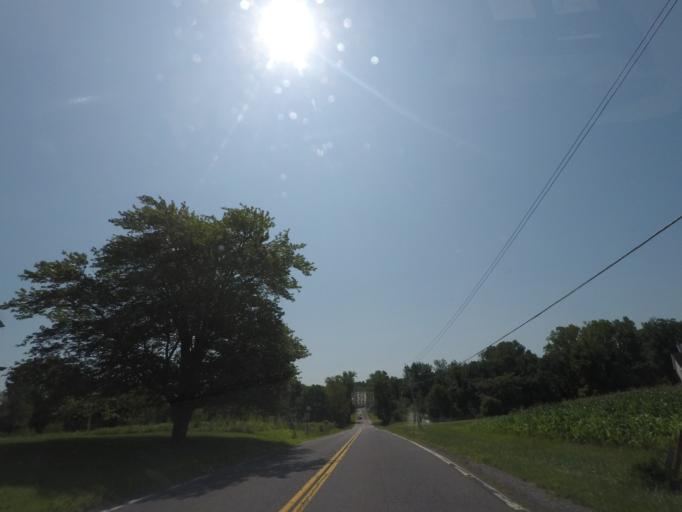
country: US
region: New York
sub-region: Saratoga County
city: Mechanicville
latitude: 42.8578
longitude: -73.7220
